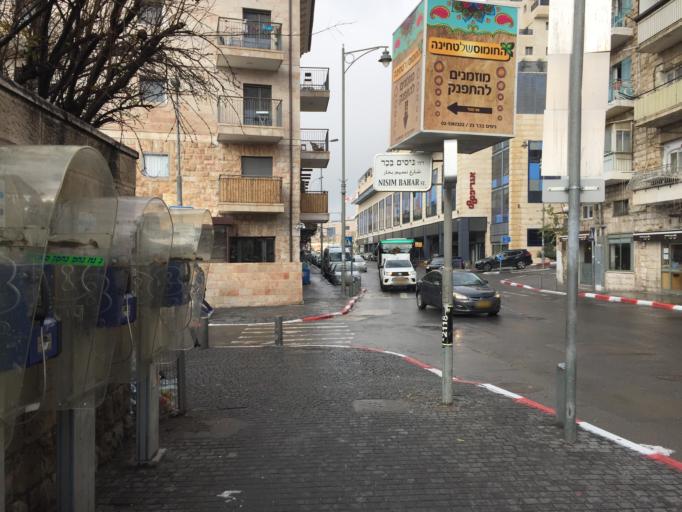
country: IL
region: Jerusalem
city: West Jerusalem
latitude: 31.7848
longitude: 35.2108
